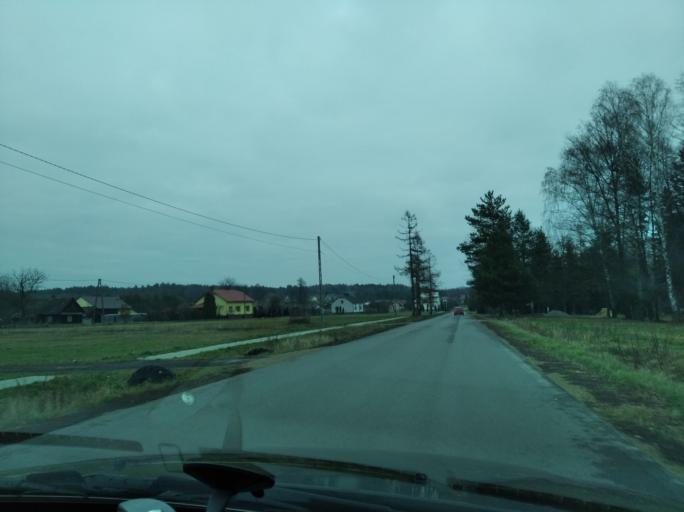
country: PL
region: Subcarpathian Voivodeship
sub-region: Powiat lancucki
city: Rakszawa
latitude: 50.1628
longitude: 22.1928
